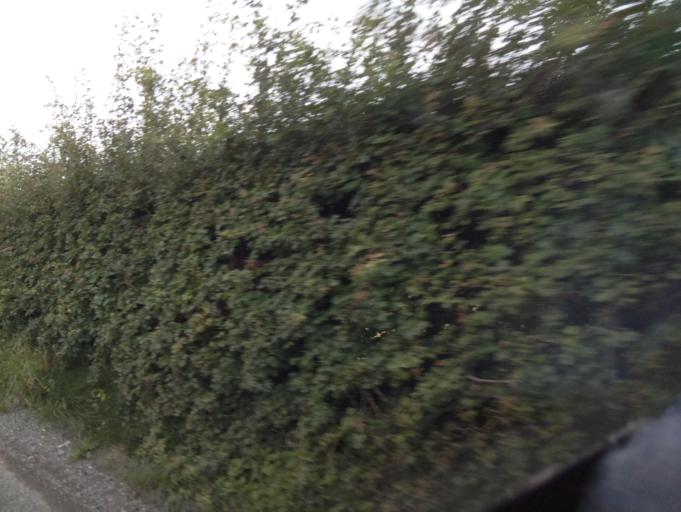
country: GB
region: England
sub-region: North Somerset
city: Winford
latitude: 51.3947
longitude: -2.6677
